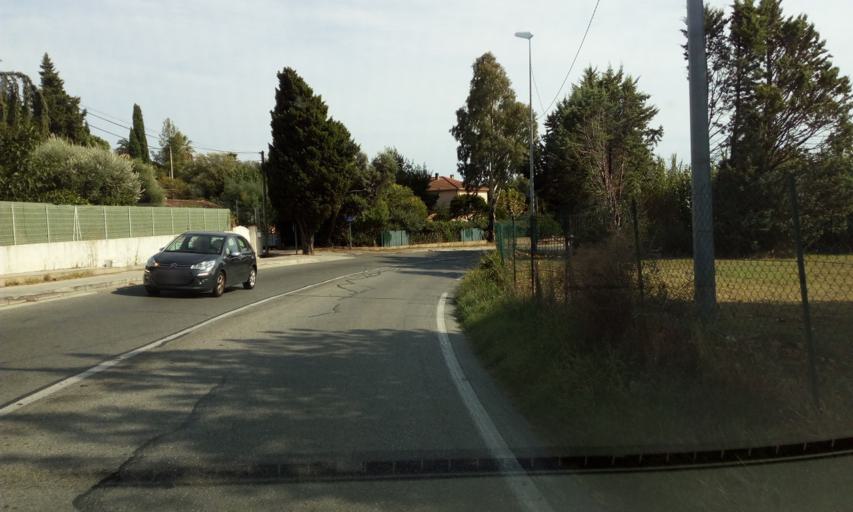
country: FR
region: Provence-Alpes-Cote d'Azur
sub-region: Departement du Var
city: Bormes-les-Mimosas
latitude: 43.1412
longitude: 6.3499
